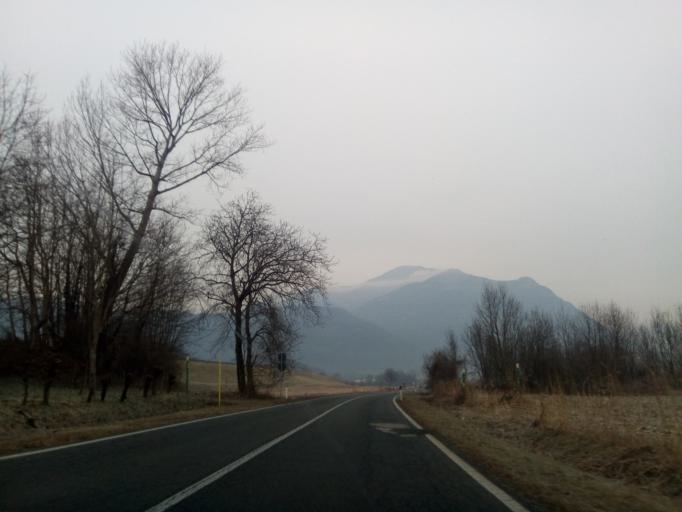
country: IT
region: Piedmont
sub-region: Provincia di Torino
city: Salerano Canavese
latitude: 45.4652
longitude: 7.8445
